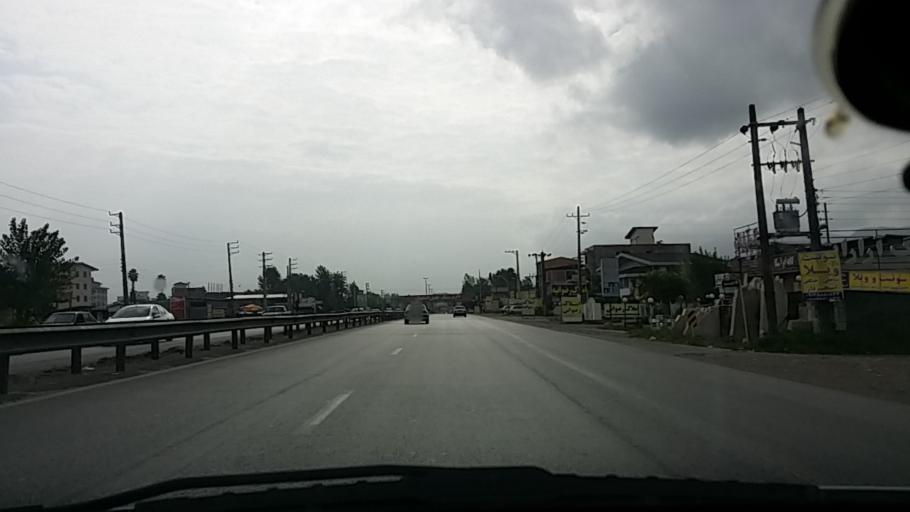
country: IR
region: Mazandaran
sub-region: Nowshahr
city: Nowshahr
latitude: 36.6389
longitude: 51.4855
